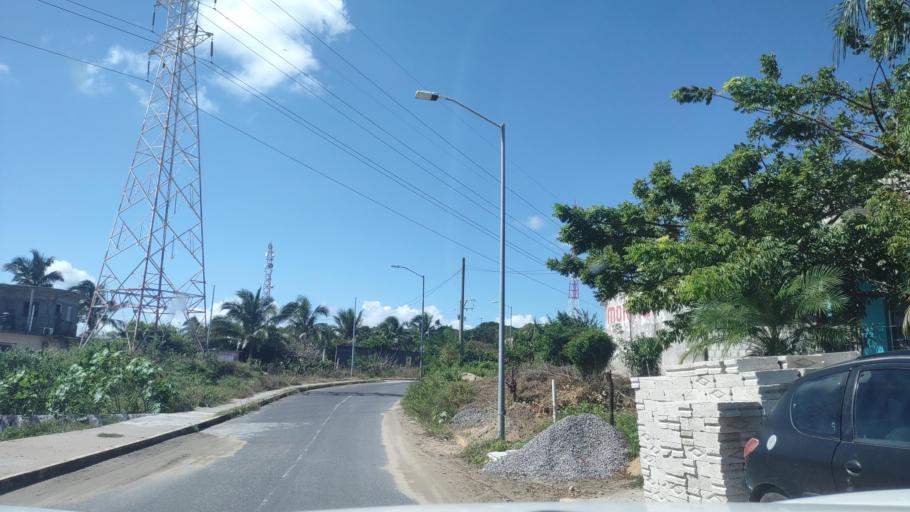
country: MX
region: Veracruz
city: Heroica Alvarado
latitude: 18.7782
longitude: -95.7629
